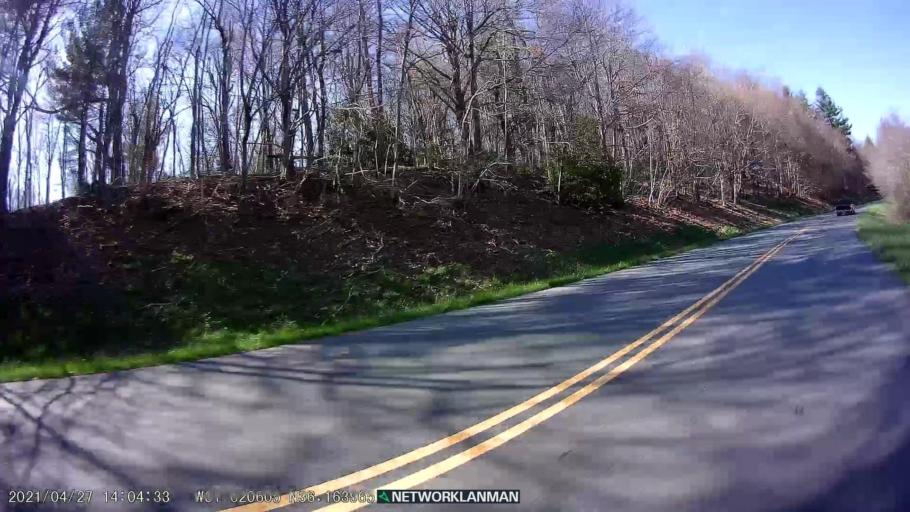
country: US
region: North Carolina
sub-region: Watauga County
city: Blowing Rock
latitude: 36.1642
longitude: -81.6204
